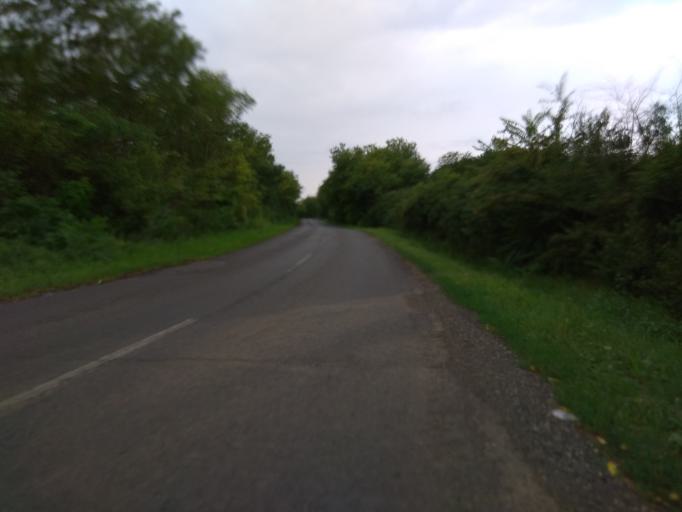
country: HU
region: Borsod-Abauj-Zemplen
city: Monok
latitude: 48.1734
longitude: 21.1163
